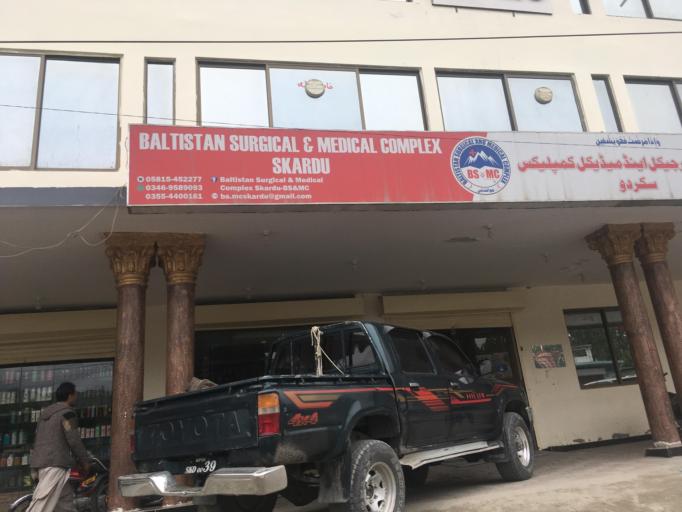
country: PK
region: Gilgit-Baltistan
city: Skardu
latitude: 35.2846
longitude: 75.6444
